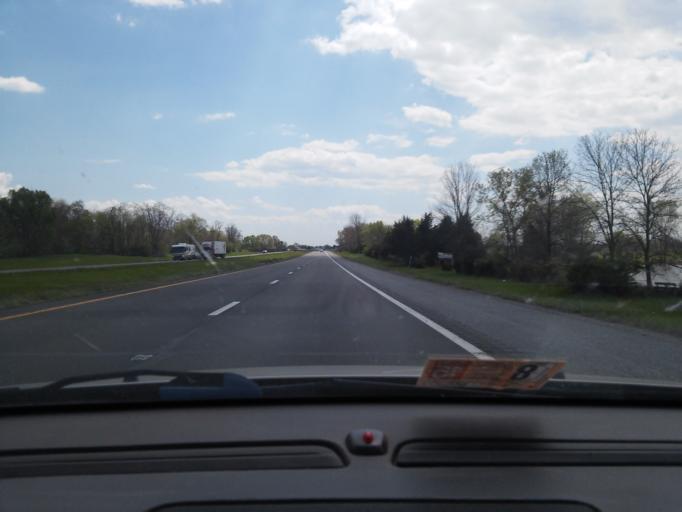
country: US
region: West Virginia
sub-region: Berkeley County
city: Inwood
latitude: 39.3066
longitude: -78.0791
